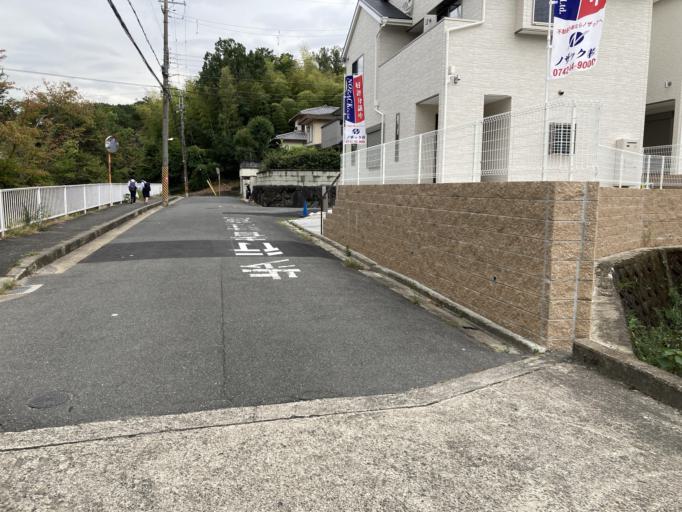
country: JP
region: Nara
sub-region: Ikoma-shi
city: Ikoma
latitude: 34.6838
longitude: 135.6985
